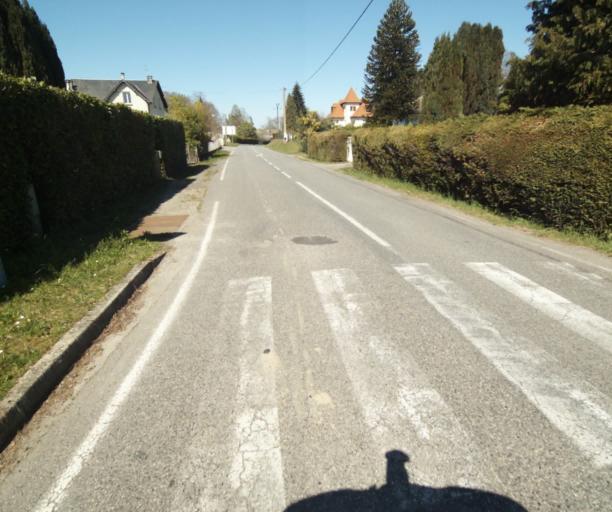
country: FR
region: Limousin
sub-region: Departement de la Correze
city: Saint-Mexant
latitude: 45.2724
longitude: 1.6662
